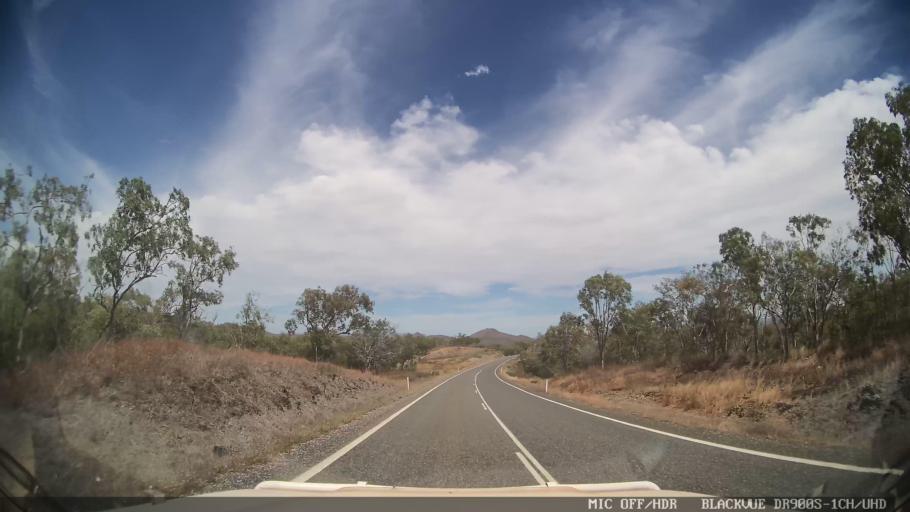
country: AU
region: Queensland
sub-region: Cook
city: Cooktown
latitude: -16.0239
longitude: 144.8114
